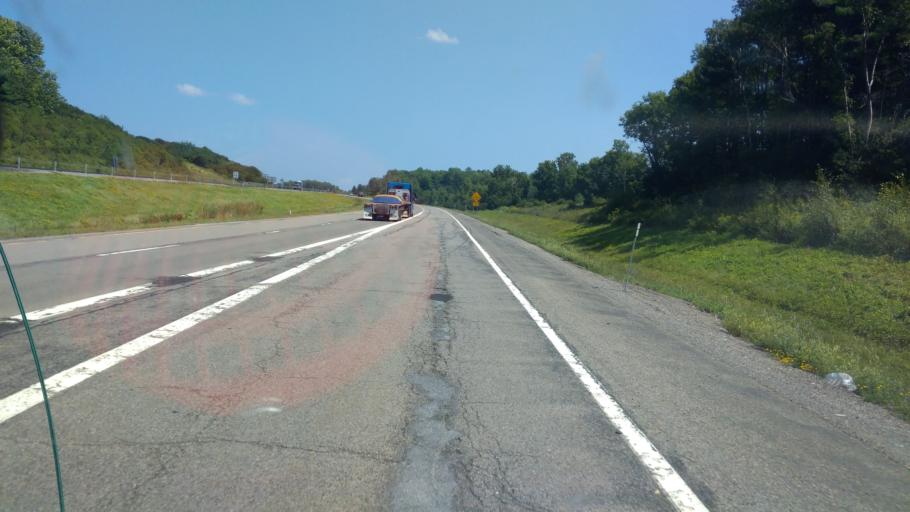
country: US
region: New York
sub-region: Allegany County
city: Alfred
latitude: 42.3061
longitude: -77.8719
